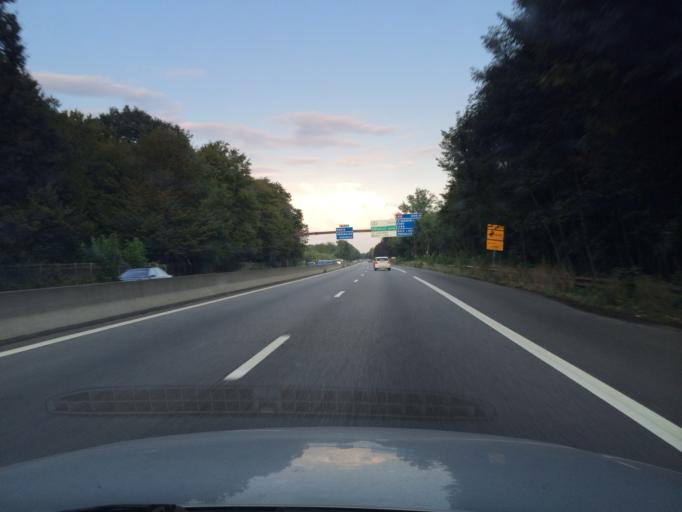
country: FR
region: Ile-de-France
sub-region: Departement des Yvelines
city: Bailly
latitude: 48.8482
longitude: 2.0746
